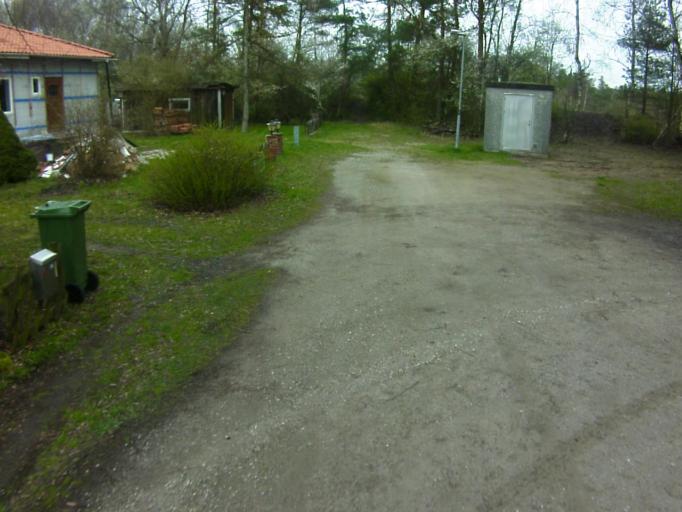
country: SE
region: Skane
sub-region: Kavlinge Kommun
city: Kaevlinge
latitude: 55.7707
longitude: 13.0738
